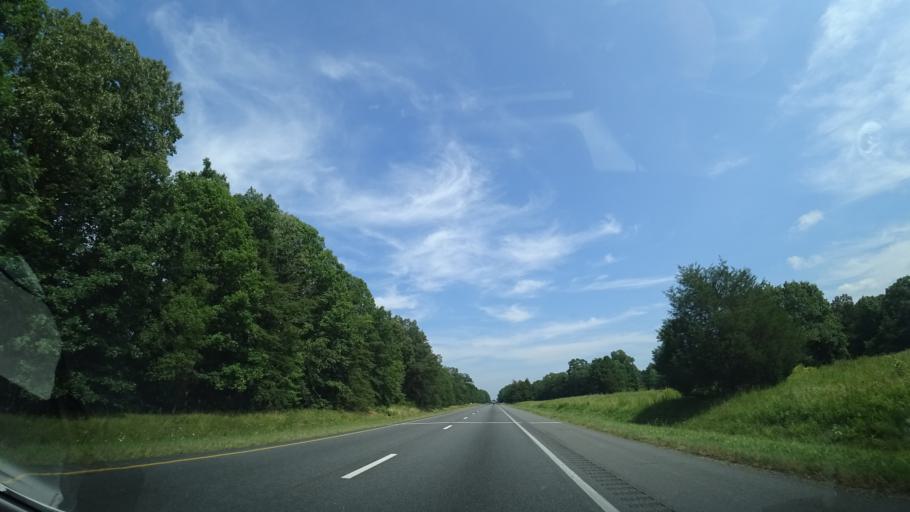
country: US
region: Virginia
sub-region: Louisa County
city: Louisa
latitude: 37.9117
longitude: -78.0661
